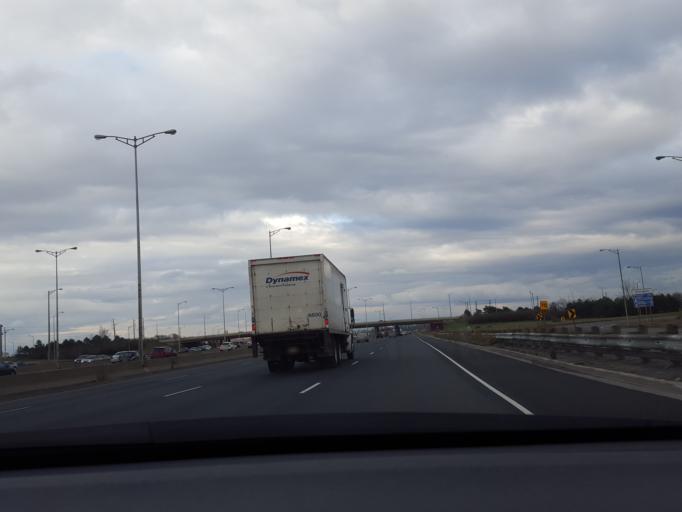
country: CA
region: Ontario
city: Mississauga
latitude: 43.6462
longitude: -79.6414
